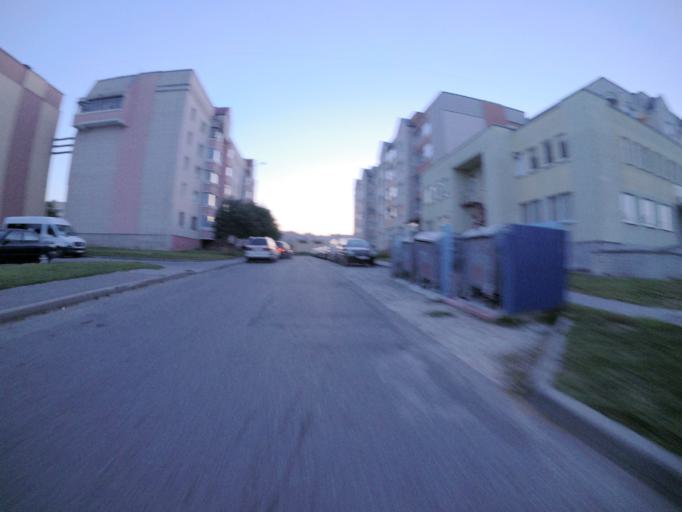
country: BY
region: Grodnenskaya
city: Hrodna
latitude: 53.7126
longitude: 23.8580
